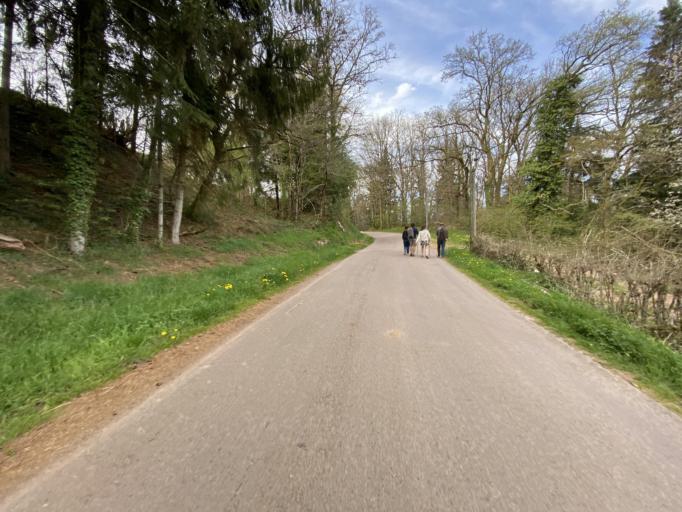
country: FR
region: Bourgogne
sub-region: Departement de la Cote-d'Or
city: Saulieu
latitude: 47.3195
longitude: 4.0945
